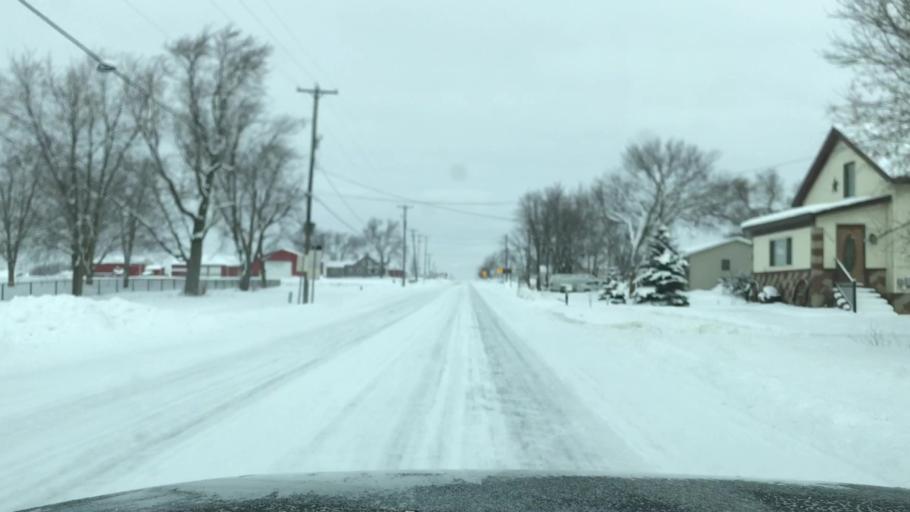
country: US
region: Michigan
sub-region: Ottawa County
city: Hudsonville
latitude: 42.8311
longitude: -85.8421
